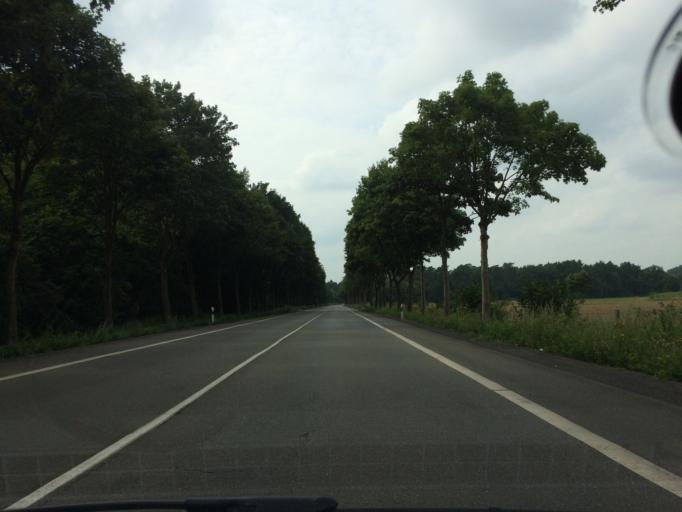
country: DE
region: North Rhine-Westphalia
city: Marl
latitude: 51.7102
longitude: 7.0582
